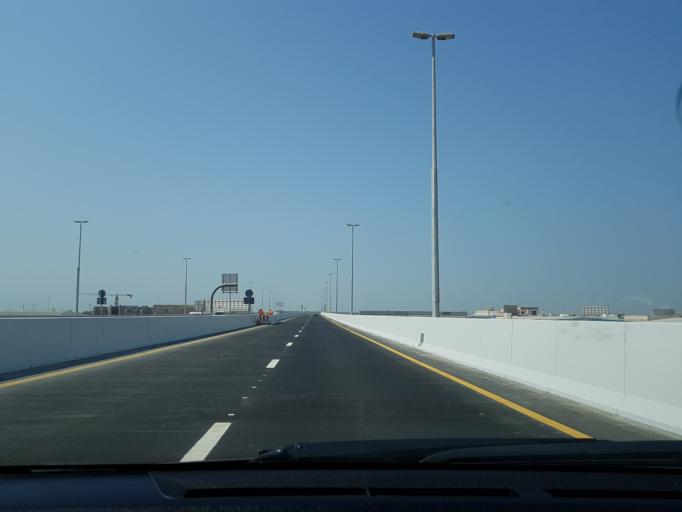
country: AE
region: Dubai
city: Dubai
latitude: 25.1566
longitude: 55.2339
